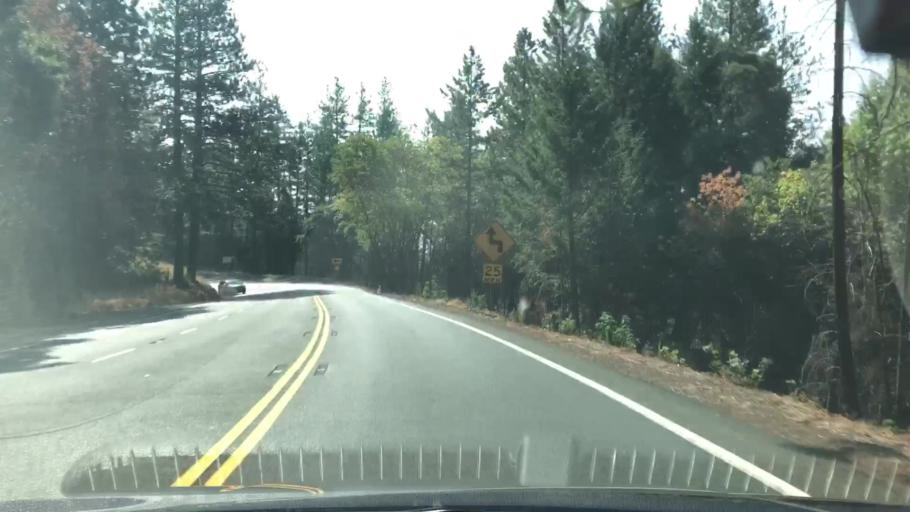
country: US
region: California
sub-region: Napa County
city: Calistoga
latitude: 38.6493
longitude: -122.5973
